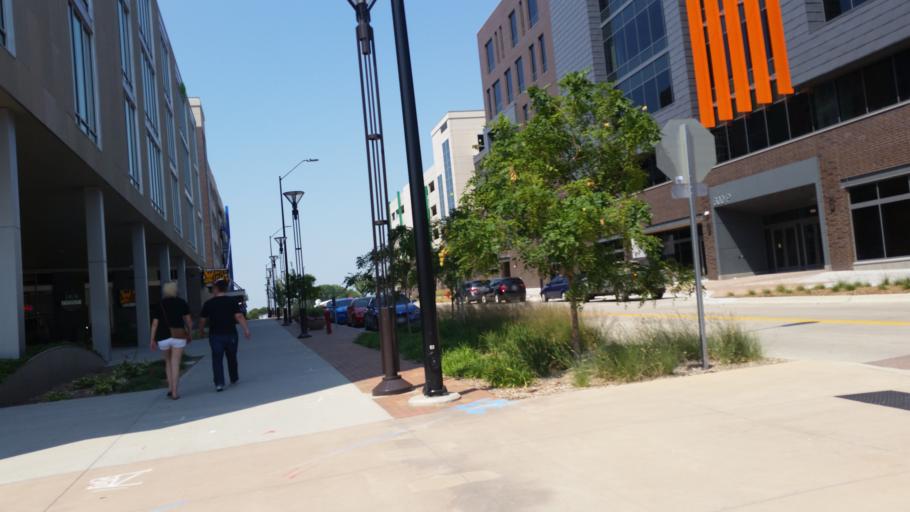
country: US
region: Nebraska
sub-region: Lancaster County
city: Lincoln
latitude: 40.8146
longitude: -96.7118
